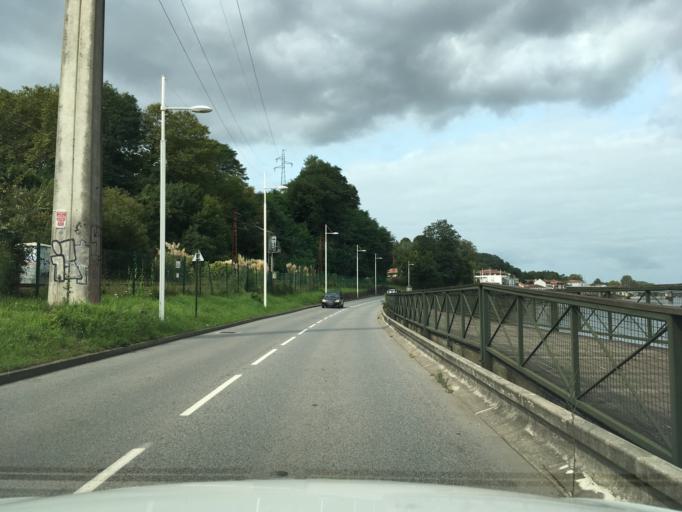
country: FR
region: Aquitaine
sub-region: Departement des Pyrenees-Atlantiques
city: Bayonne
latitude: 43.4836
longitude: -1.4546
